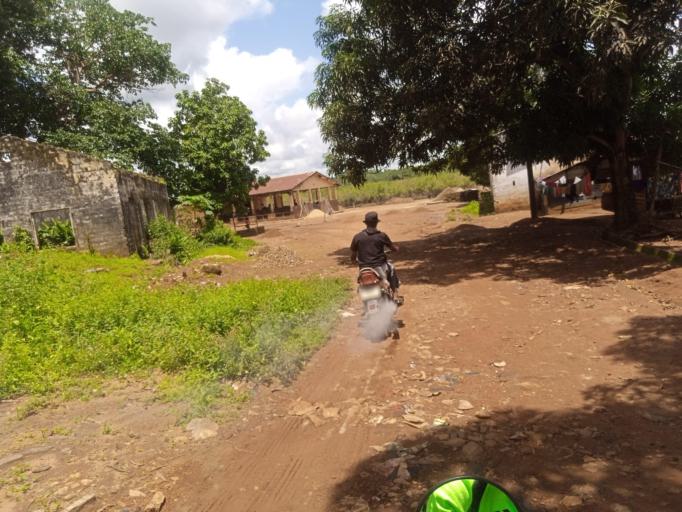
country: SL
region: Northern Province
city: Port Loko
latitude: 8.7638
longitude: -12.7918
